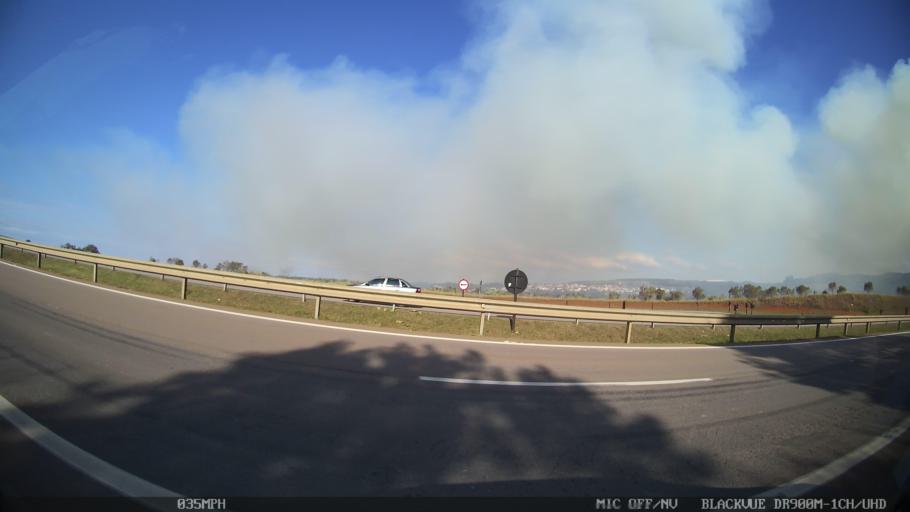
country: BR
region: Sao Paulo
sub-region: Piracicaba
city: Piracicaba
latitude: -22.6936
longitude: -47.6022
